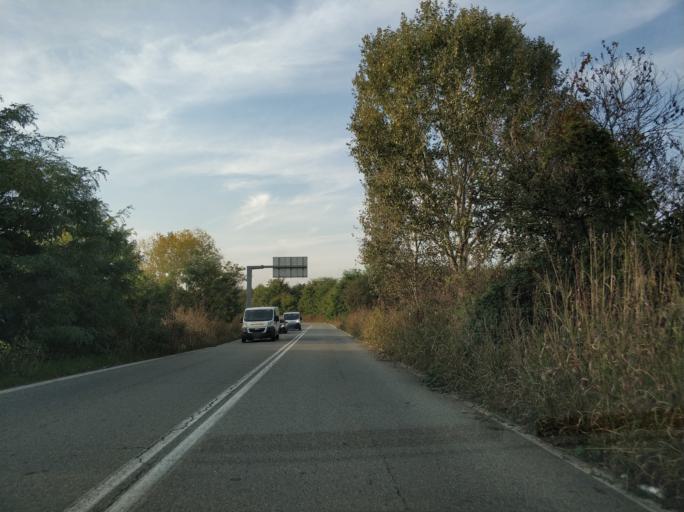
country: IT
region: Piedmont
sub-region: Provincia di Torino
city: Borgaro Torinese
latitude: 45.1389
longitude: 7.6951
